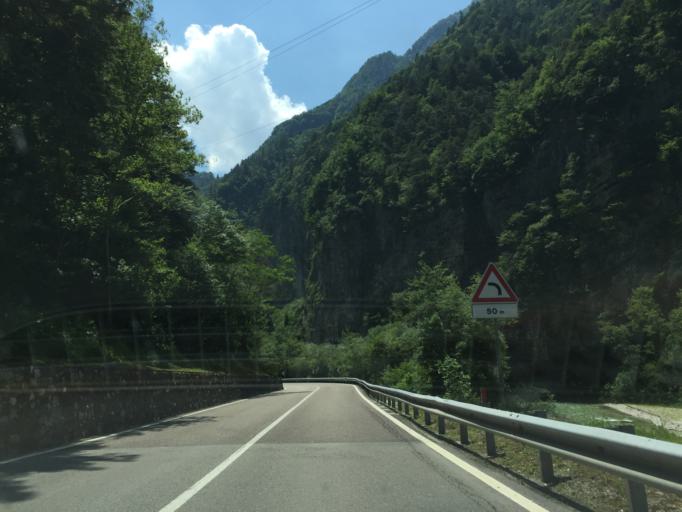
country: IT
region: Trentino-Alto Adige
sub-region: Provincia di Trento
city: Imer
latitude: 46.1300
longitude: 11.7692
